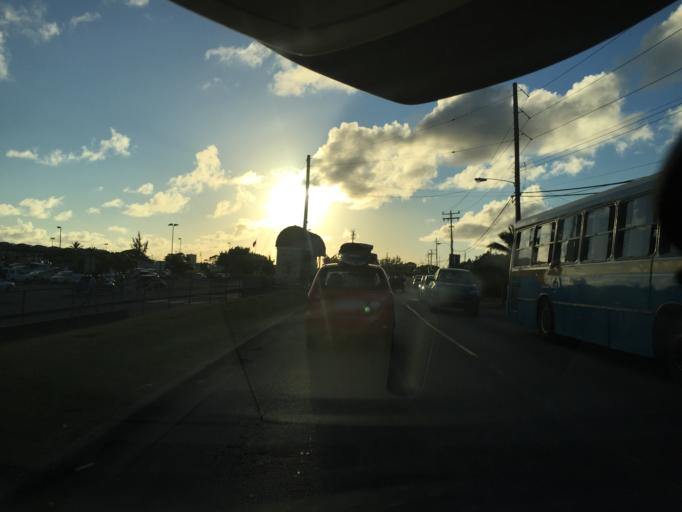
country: BB
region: Saint Philip
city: Crane
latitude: 13.0813
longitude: -59.4882
